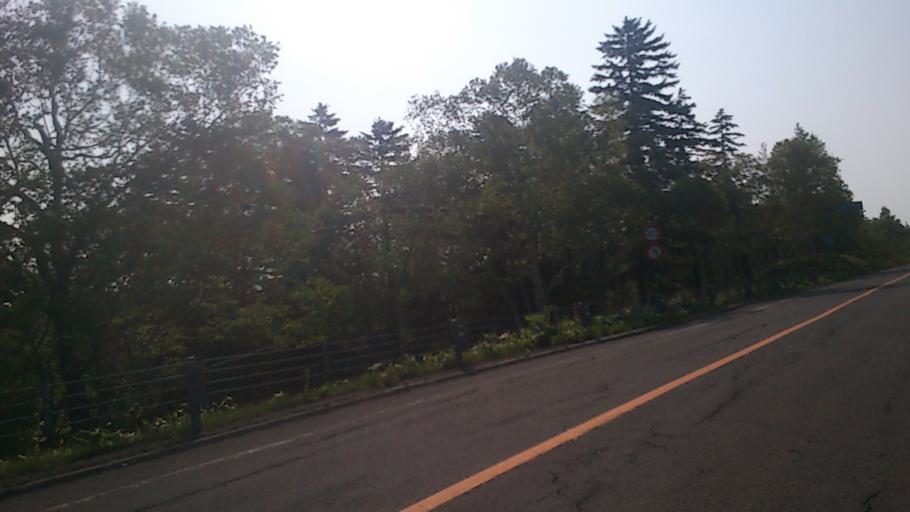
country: JP
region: Hokkaido
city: Bihoro
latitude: 43.4482
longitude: 144.2053
